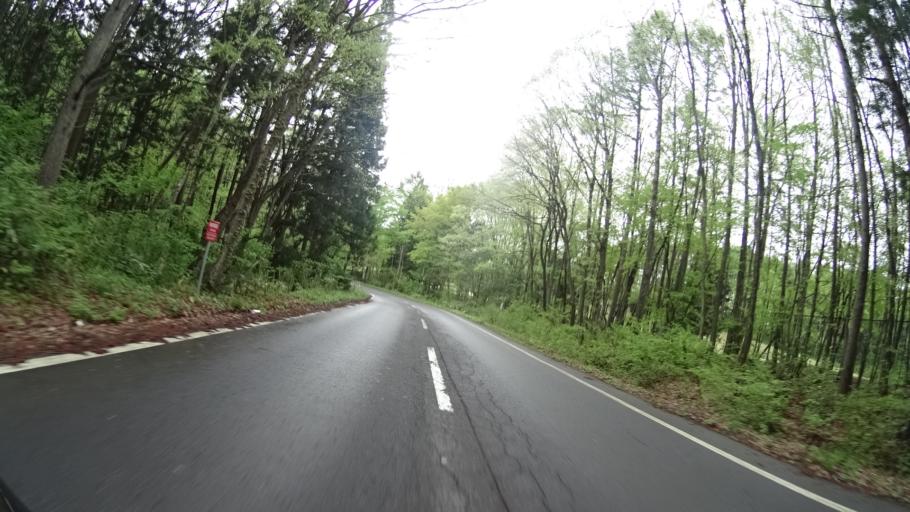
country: JP
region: Nagano
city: Nagano-shi
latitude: 36.7513
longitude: 138.2027
